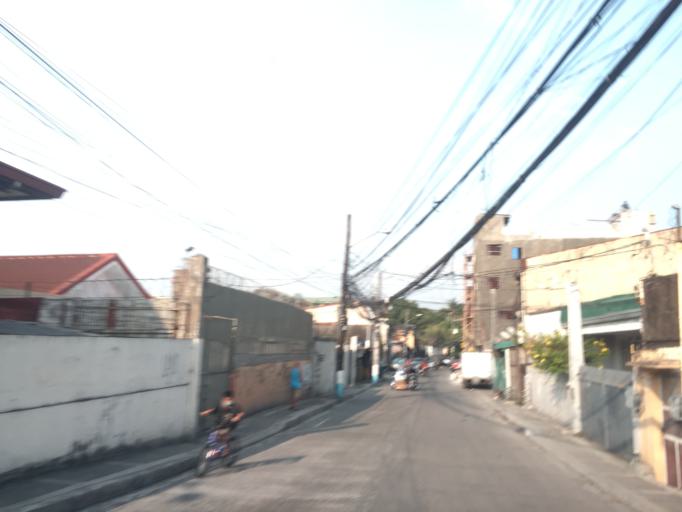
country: PH
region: Calabarzon
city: Bagong Pagasa
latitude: 14.6634
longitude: 121.0182
